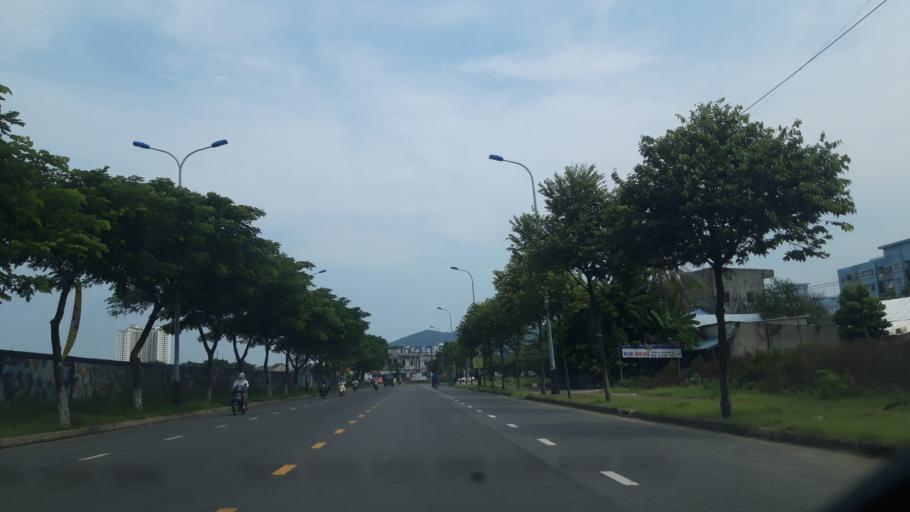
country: VN
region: Da Nang
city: Da Nang
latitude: 16.0868
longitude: 108.2289
